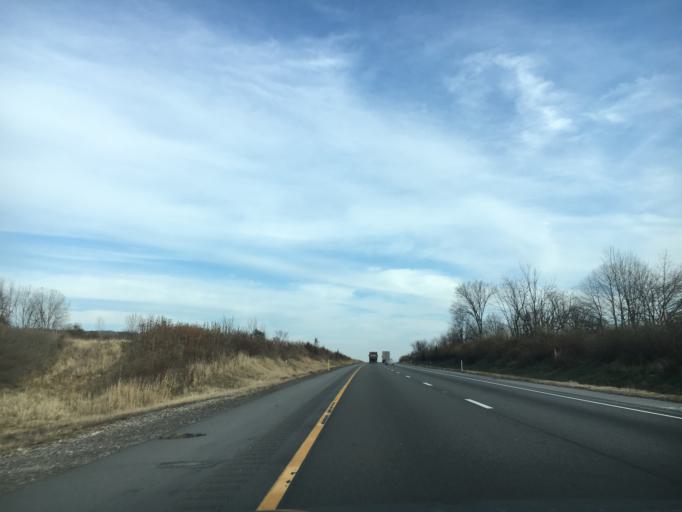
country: US
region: Pennsylvania
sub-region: Montour County
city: Danville
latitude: 40.9999
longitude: -76.6241
